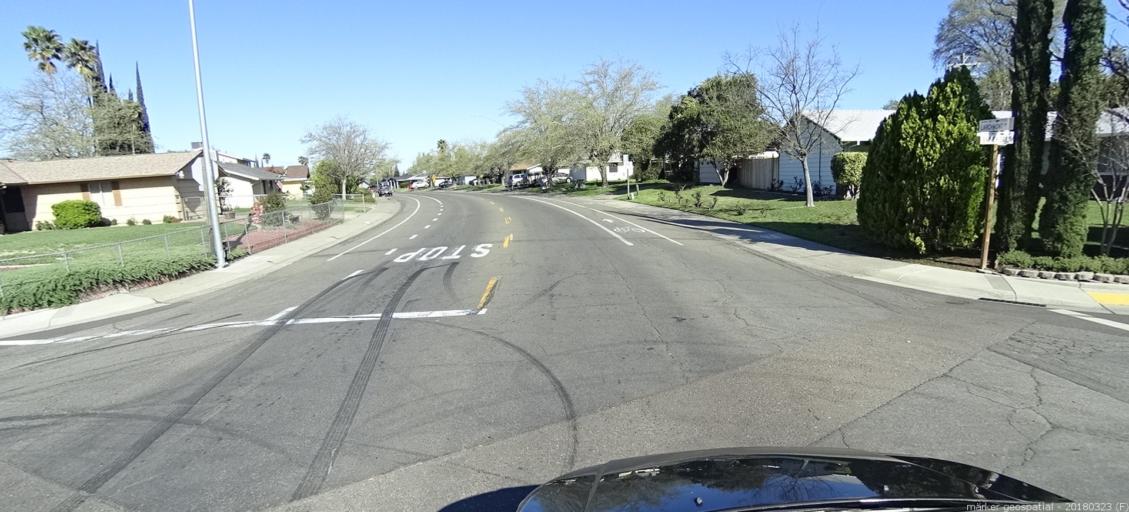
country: US
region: California
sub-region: Sacramento County
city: North Highlands
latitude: 38.7010
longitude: -121.3778
